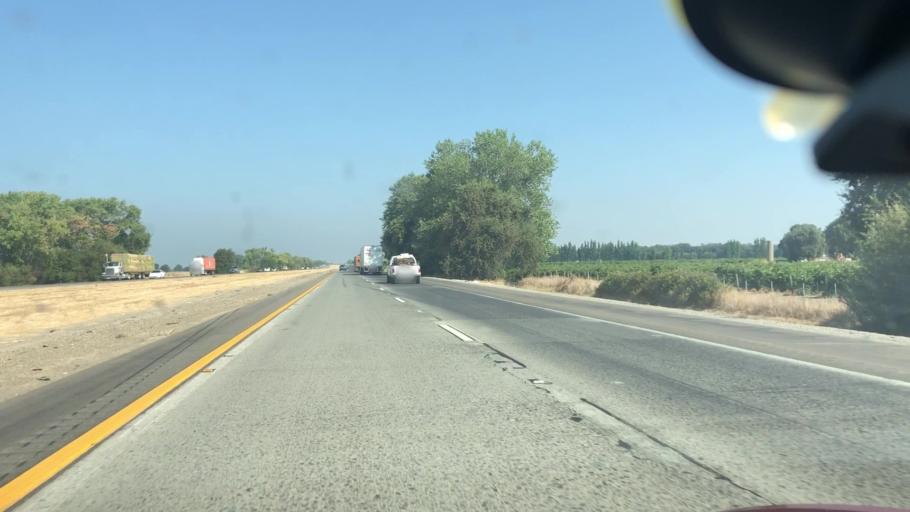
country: US
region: California
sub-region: San Joaquin County
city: Thornton
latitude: 38.2127
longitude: -121.4212
